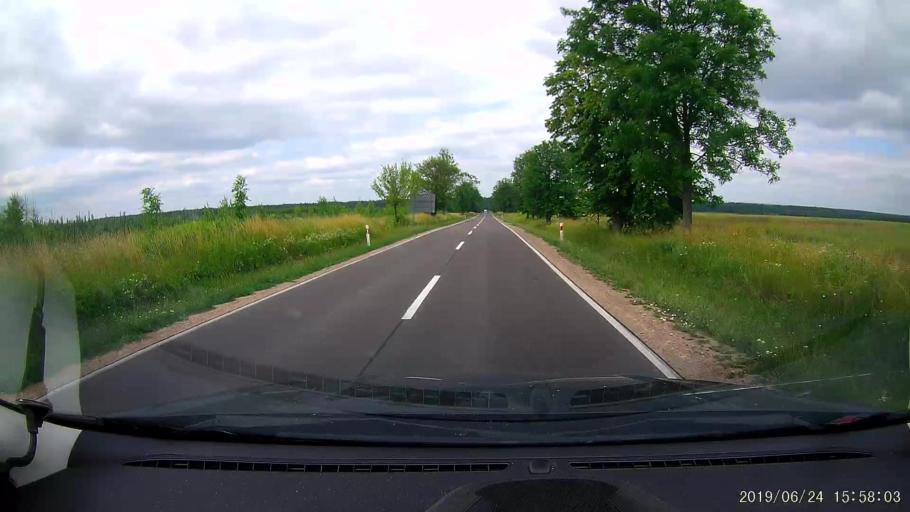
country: PL
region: Subcarpathian Voivodeship
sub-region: Powiat lubaczowski
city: Cieszanow
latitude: 50.2569
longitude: 23.1416
